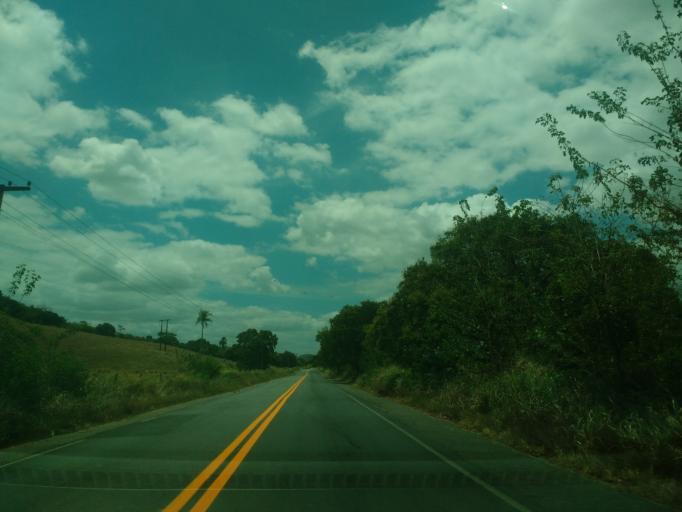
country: BR
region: Alagoas
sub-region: Uniao Dos Palmares
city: Uniao dos Palmares
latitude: -9.1416
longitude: -36.0432
